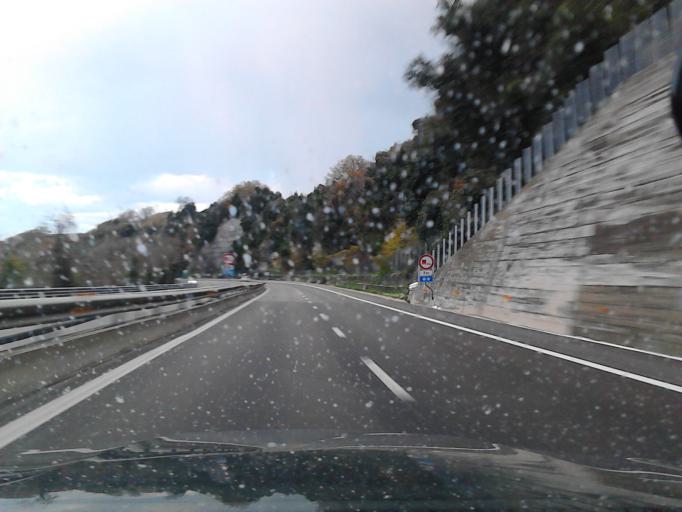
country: IT
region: Abruzzo
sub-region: Provincia di Chieti
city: Treglio
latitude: 42.2724
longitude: 14.4347
